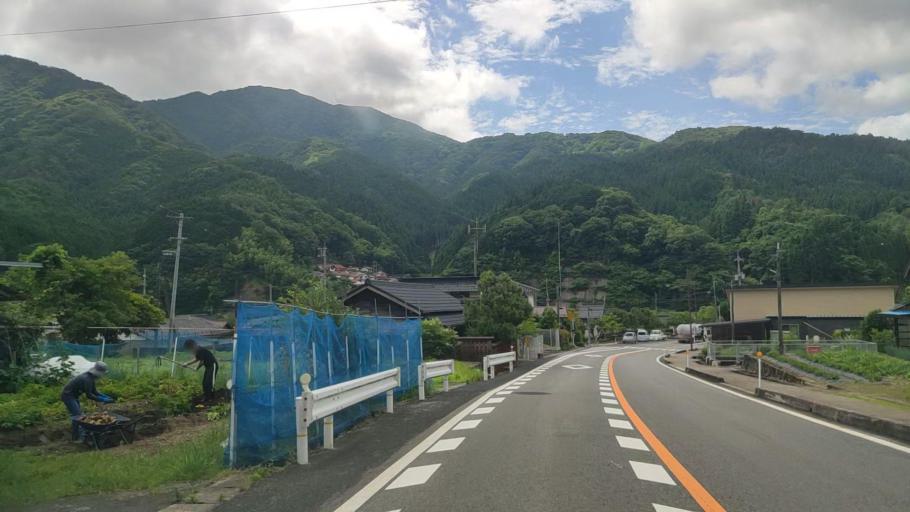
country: JP
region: Tottori
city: Yonago
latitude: 35.2459
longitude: 133.4447
